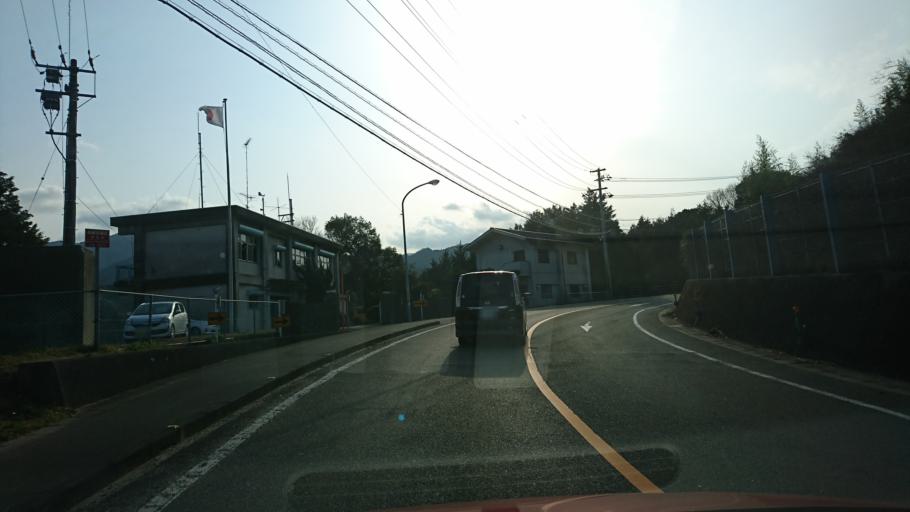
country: JP
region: Ehime
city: Hojo
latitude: 33.9943
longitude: 132.9315
